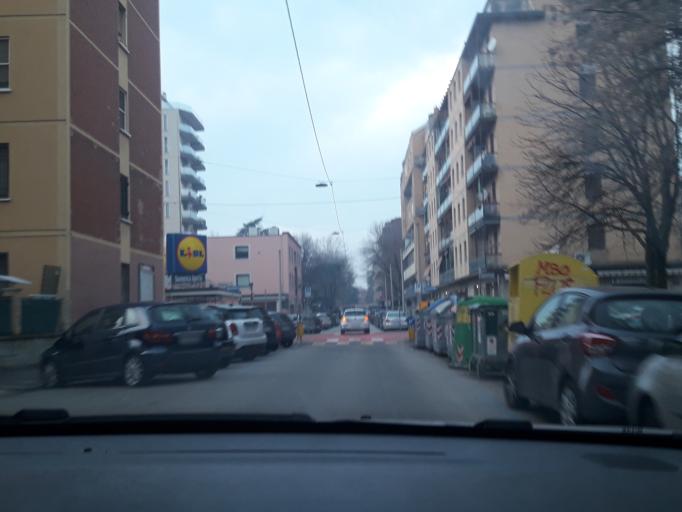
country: IT
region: Emilia-Romagna
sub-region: Provincia di Bologna
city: Bologna
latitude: 44.5026
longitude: 11.3145
